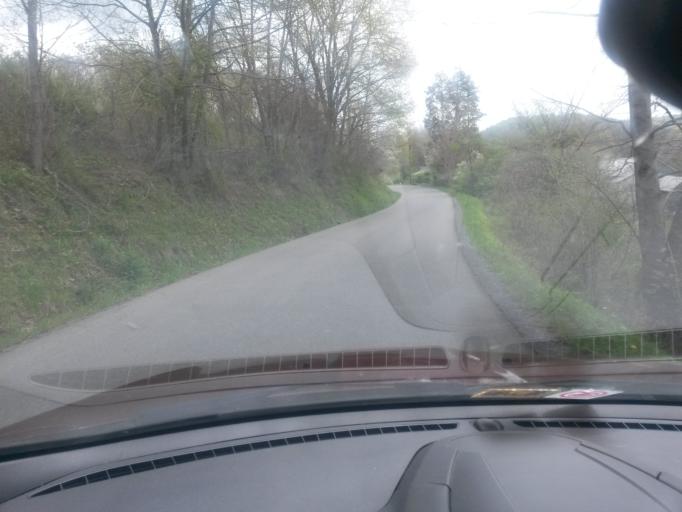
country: US
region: West Virginia
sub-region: Greenbrier County
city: White Sulphur Springs
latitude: 38.0422
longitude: -80.3464
